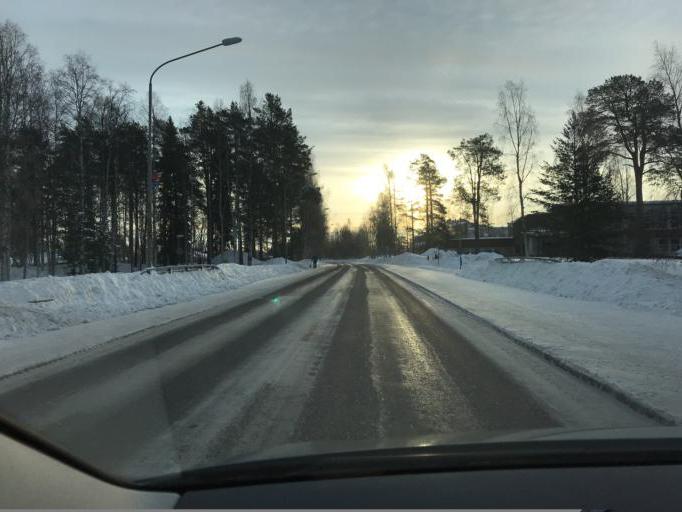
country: SE
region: Norrbotten
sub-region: Lulea Kommun
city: Bergnaset
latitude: 65.6063
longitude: 22.1105
